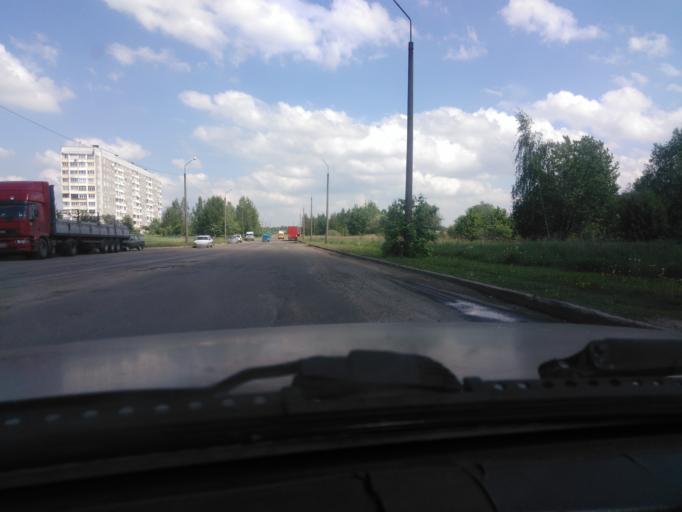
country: BY
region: Mogilev
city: Mahilyow
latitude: 53.9461
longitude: 30.3713
